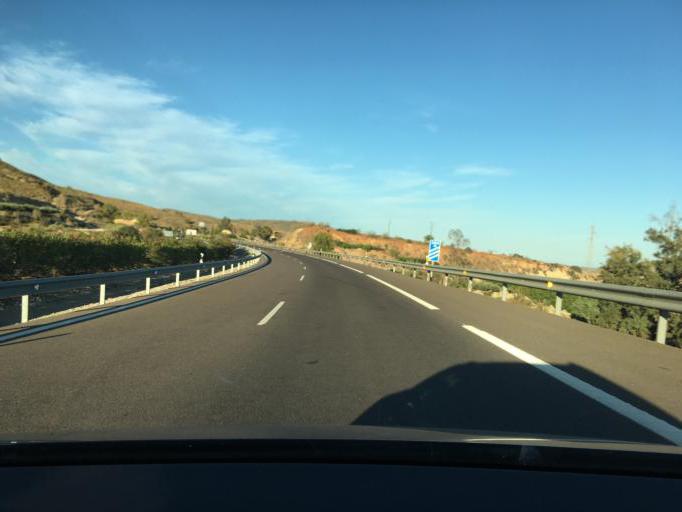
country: ES
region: Andalusia
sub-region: Provincia de Almeria
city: Bedar
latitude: 37.1434
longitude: -1.9917
